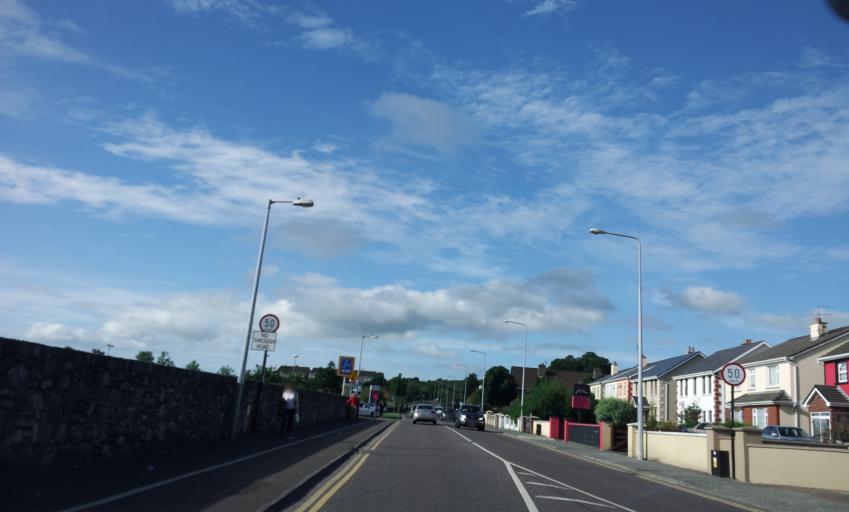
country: IE
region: Munster
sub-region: Ciarrai
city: Cill Airne
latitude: 52.0608
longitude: -9.4931
